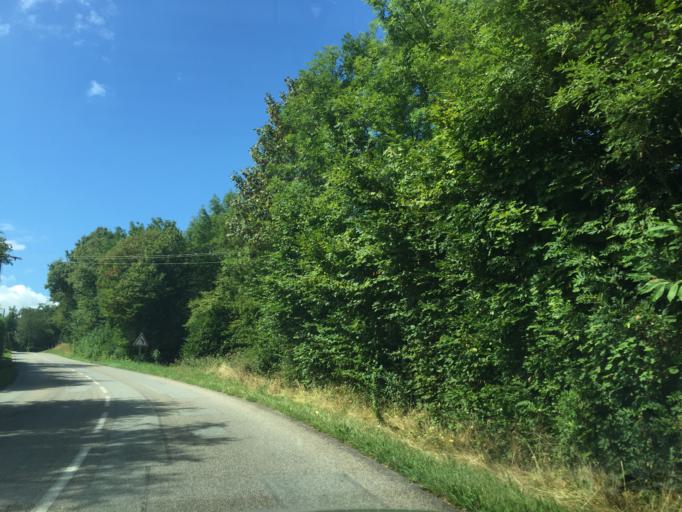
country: FR
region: Rhone-Alpes
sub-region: Departement de la Savoie
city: La Rochette
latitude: 45.4527
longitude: 6.1261
